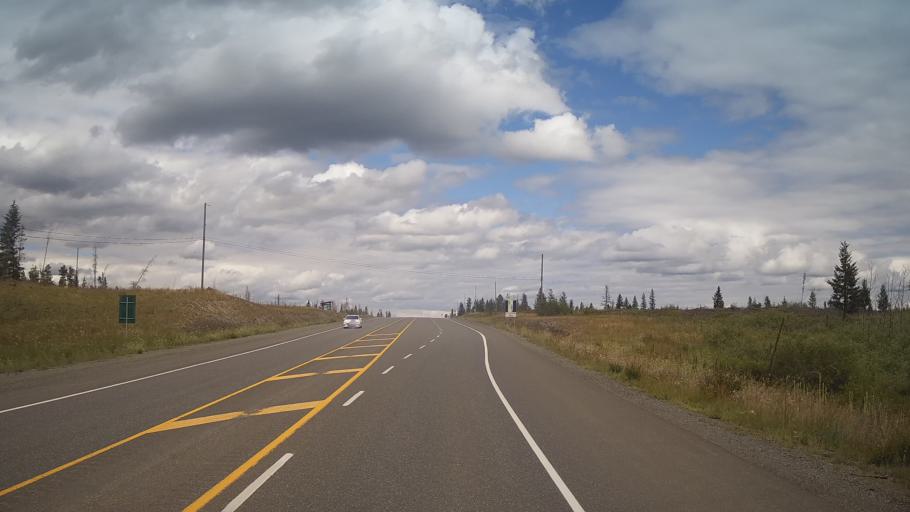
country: CA
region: British Columbia
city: Cache Creek
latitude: 51.3232
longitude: -121.3871
